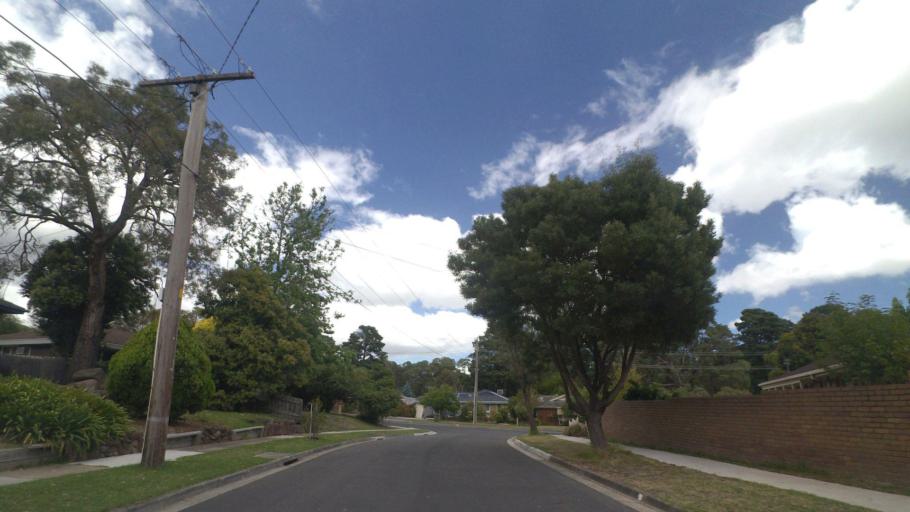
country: AU
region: Victoria
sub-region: Knox
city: Boronia
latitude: -37.8678
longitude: 145.2950
